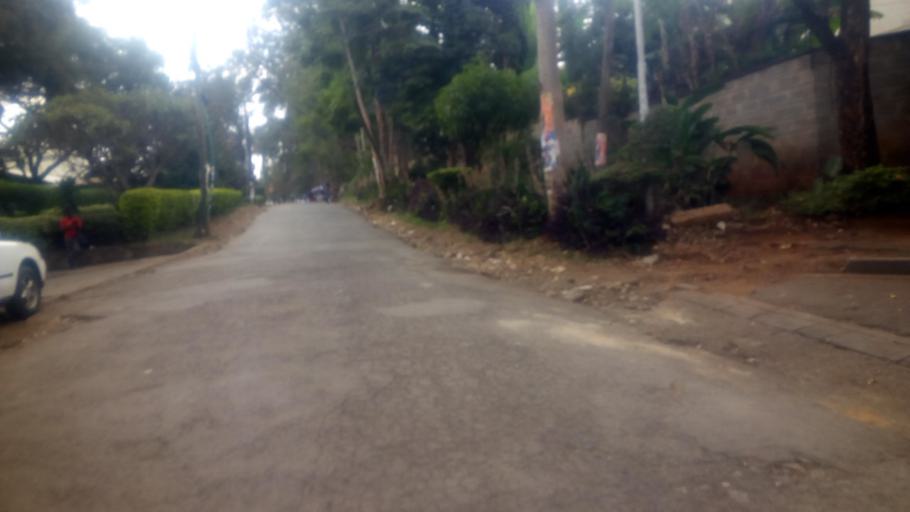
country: KE
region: Nairobi Area
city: Nairobi
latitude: -1.2819
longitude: 36.8119
